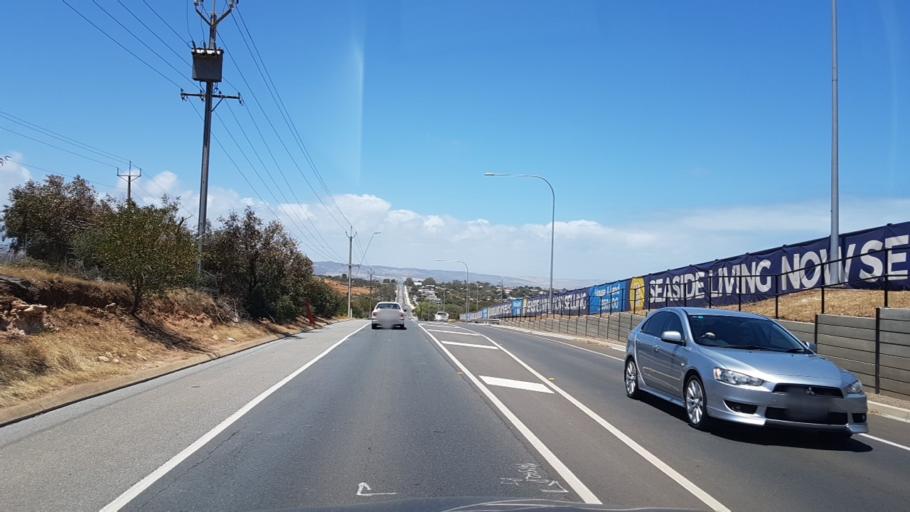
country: AU
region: South Australia
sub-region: Onkaparinga
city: Moana
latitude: -35.2176
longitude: 138.4796
